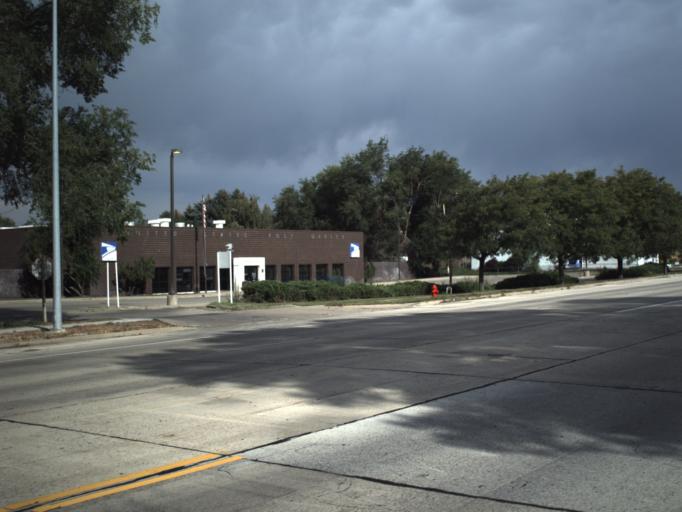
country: US
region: Utah
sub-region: Weber County
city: Harrisville
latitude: 41.2630
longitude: -111.9695
